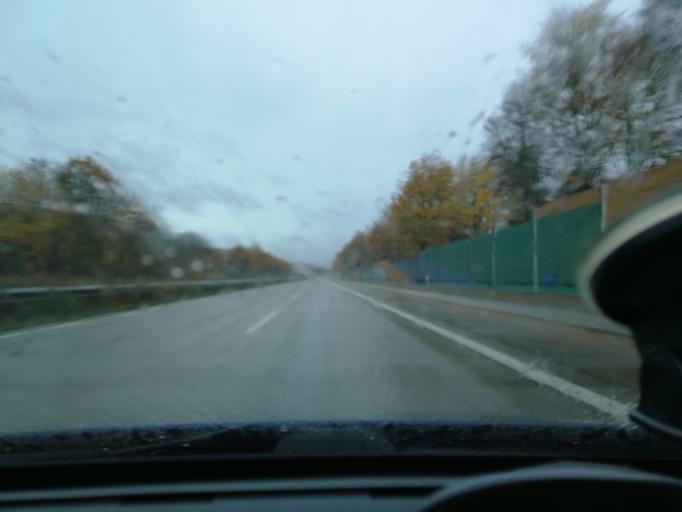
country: DE
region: Rheinland-Pfalz
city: Esch
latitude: 49.8941
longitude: 6.8519
